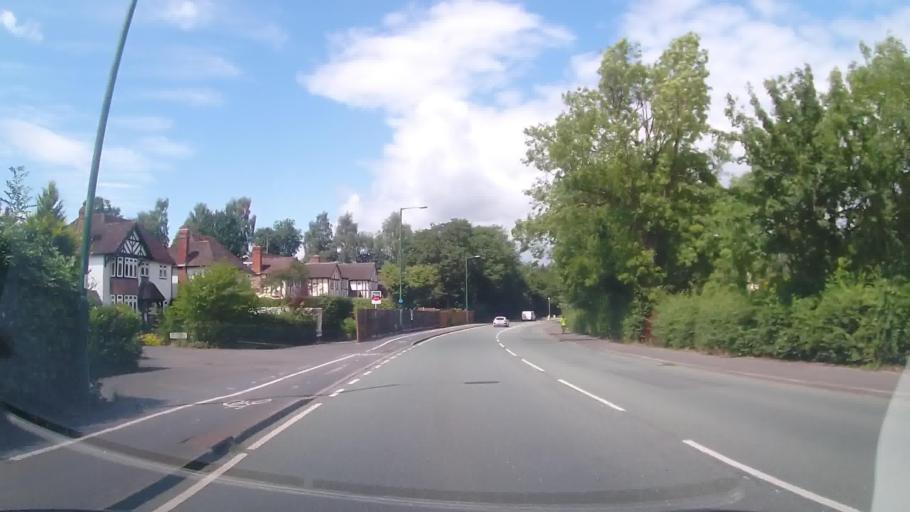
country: GB
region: England
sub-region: Shropshire
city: Shrewsbury
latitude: 52.6997
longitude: -2.7683
